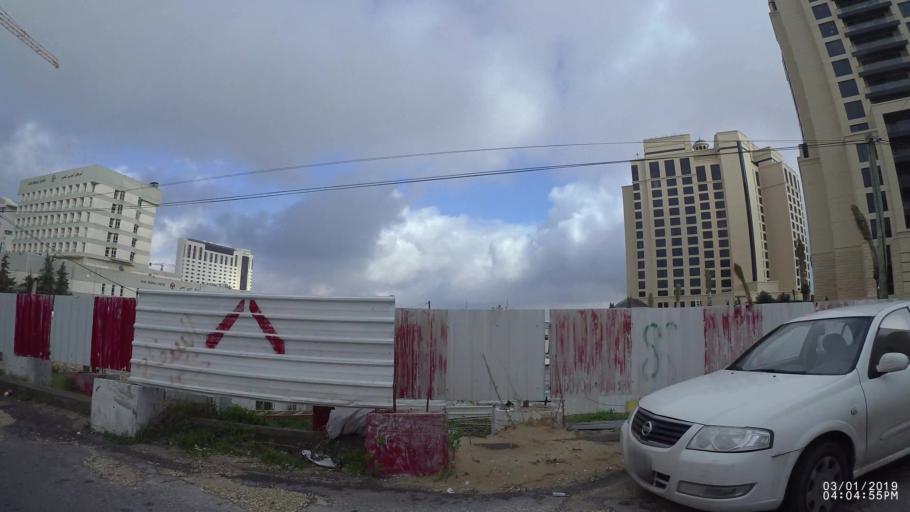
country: JO
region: Amman
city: Wadi as Sir
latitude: 31.9588
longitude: 35.8772
